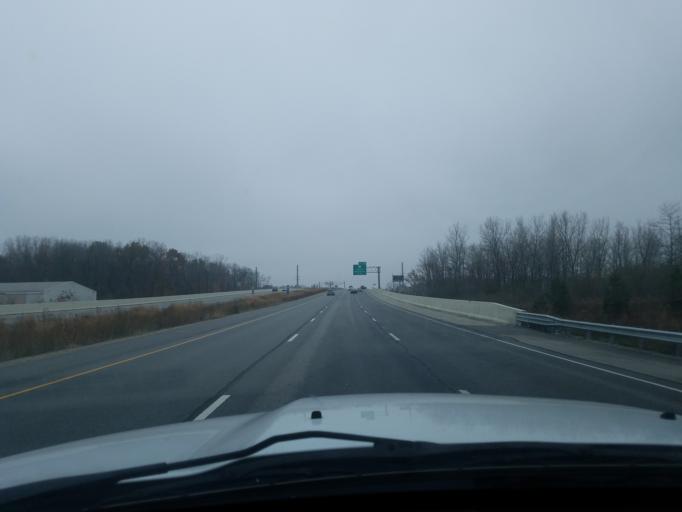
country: US
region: Indiana
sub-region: Hamilton County
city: Westfield
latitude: 40.0295
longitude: -86.1342
